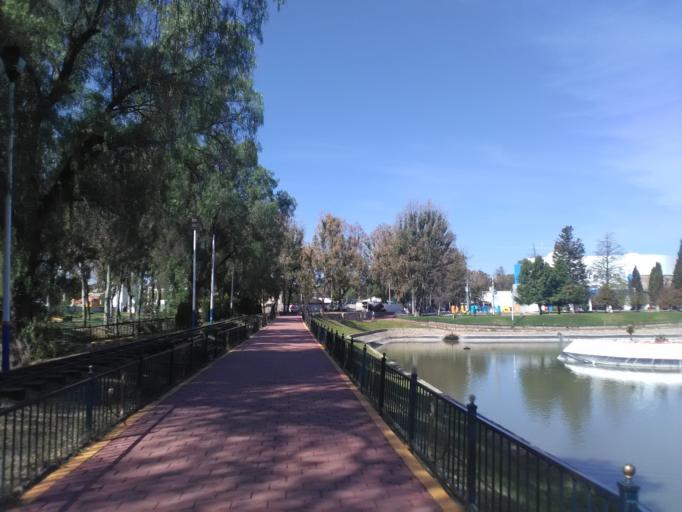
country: MX
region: Durango
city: Victoria de Durango
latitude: 24.0243
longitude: -104.6854
